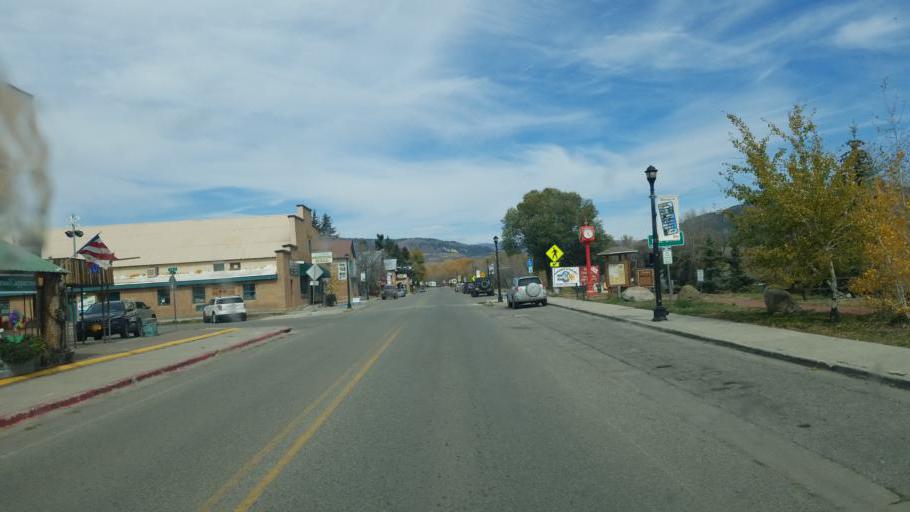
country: US
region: New Mexico
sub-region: Rio Arriba County
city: Chama
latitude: 36.9024
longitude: -106.5794
